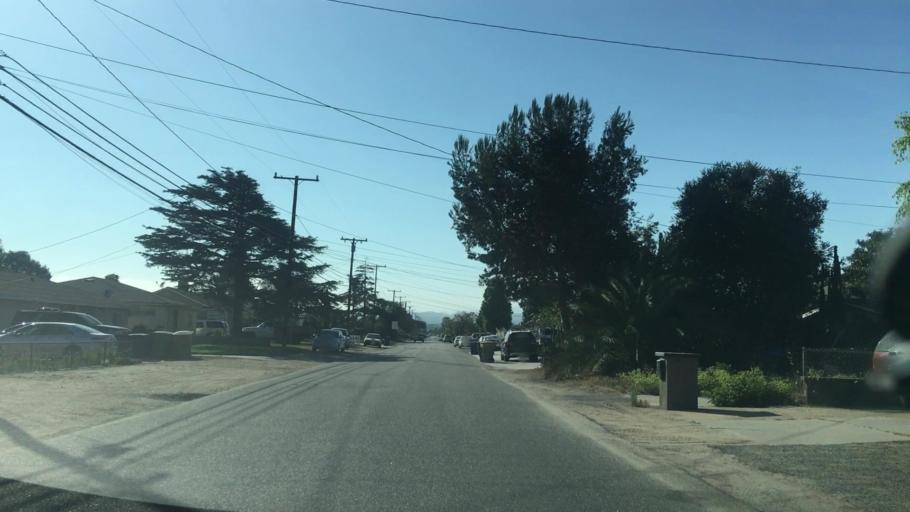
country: US
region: California
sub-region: Ventura County
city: El Rio
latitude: 34.2366
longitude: -119.1575
